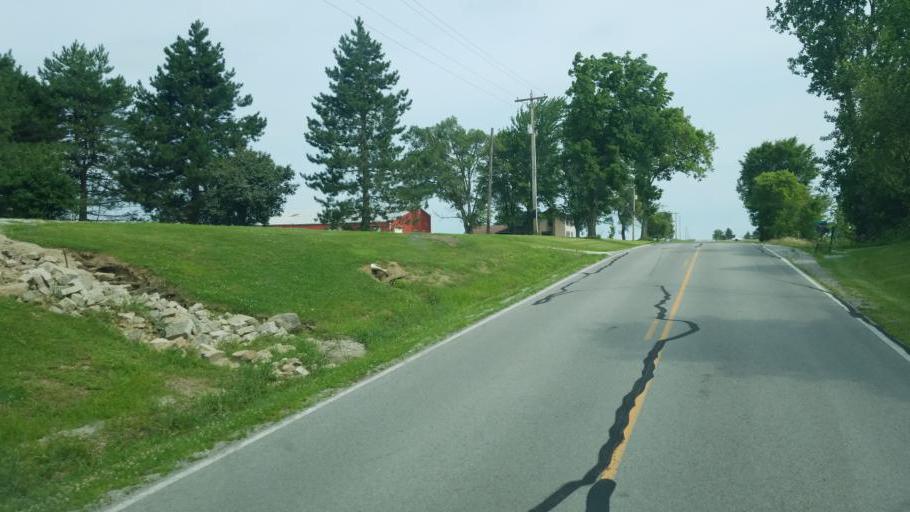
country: US
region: Ohio
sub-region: Wyandot County
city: Carey
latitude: 40.8835
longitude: -83.3807
